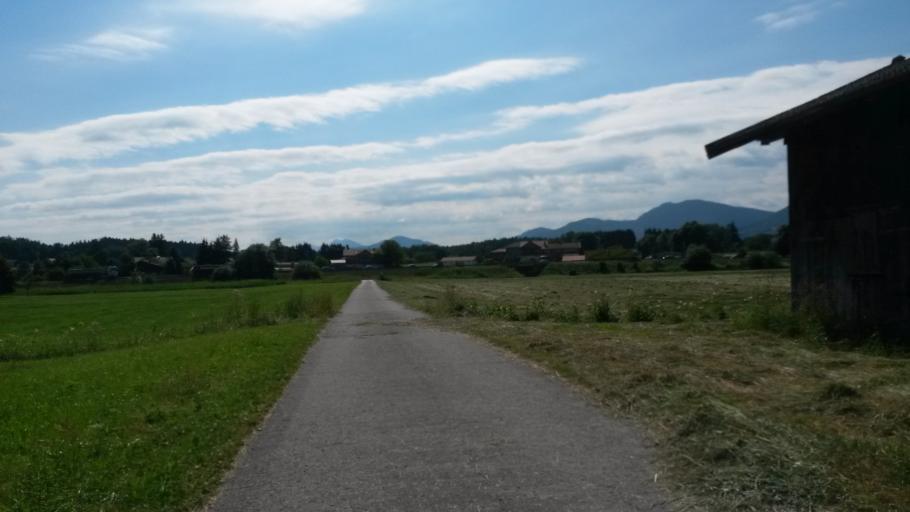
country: DE
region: Bavaria
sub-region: Upper Bavaria
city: Grabenstatt
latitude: 47.8333
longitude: 12.5212
